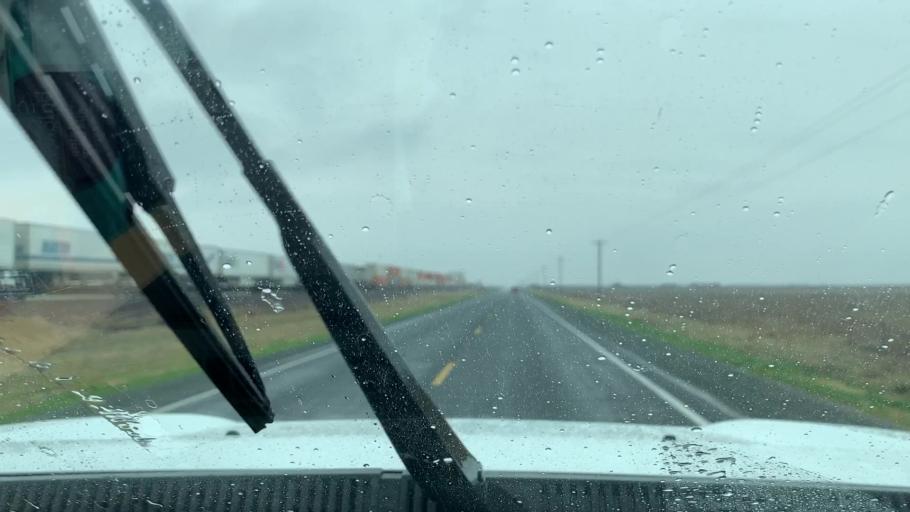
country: US
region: California
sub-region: Tulare County
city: Alpaugh
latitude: 35.9154
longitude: -119.4228
